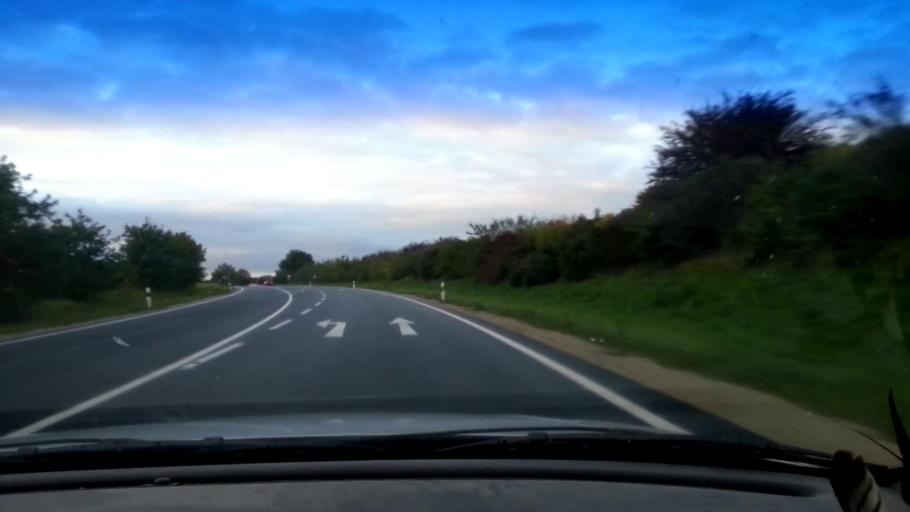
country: DE
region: Bavaria
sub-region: Upper Franconia
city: Stegaurach
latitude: 49.8607
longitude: 10.8599
